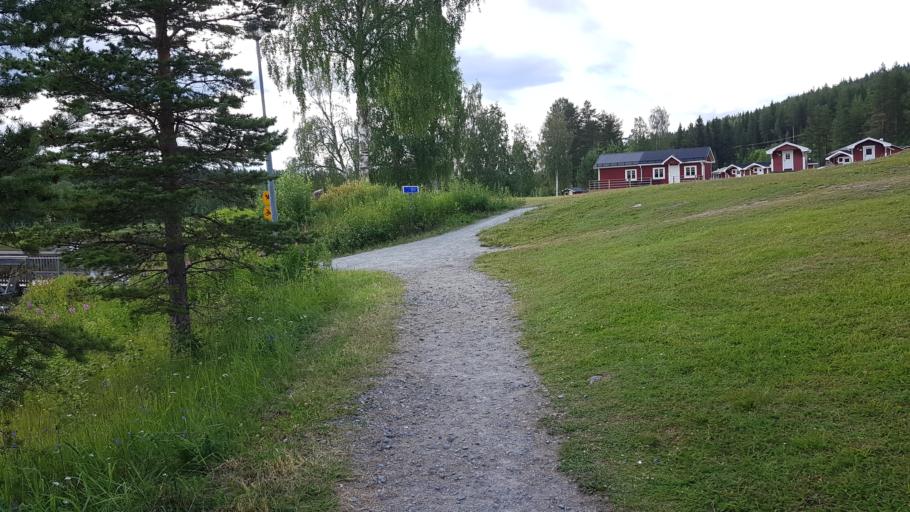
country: SE
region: Norrbotten
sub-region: Alvsbyns Kommun
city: AElvsbyn
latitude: 65.8567
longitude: 20.4199
